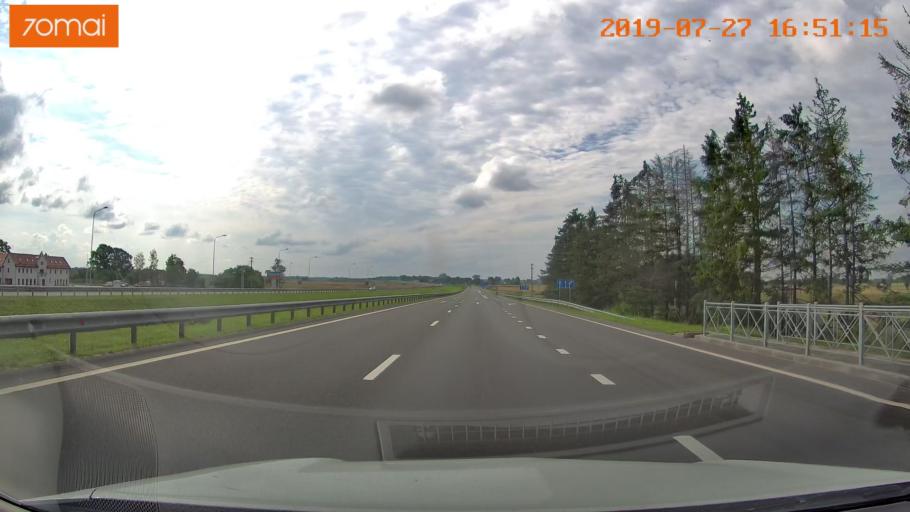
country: RU
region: Kaliningrad
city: Gvardeysk
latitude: 54.6817
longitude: 20.8918
